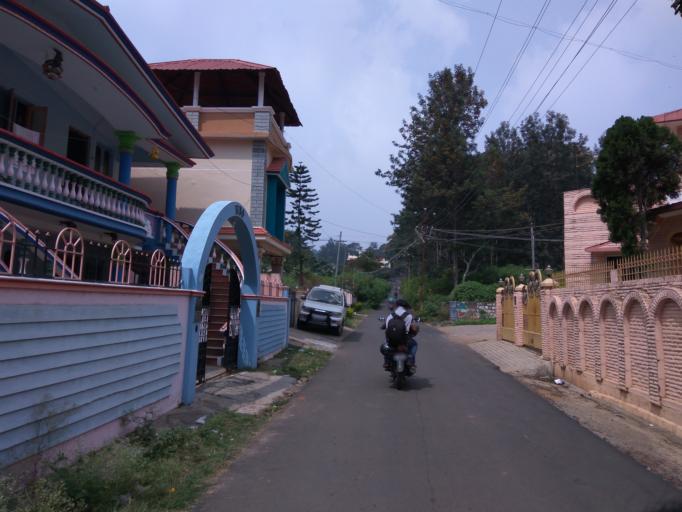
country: IN
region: Tamil Nadu
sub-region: Salem
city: Salem
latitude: 11.7721
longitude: 78.2150
